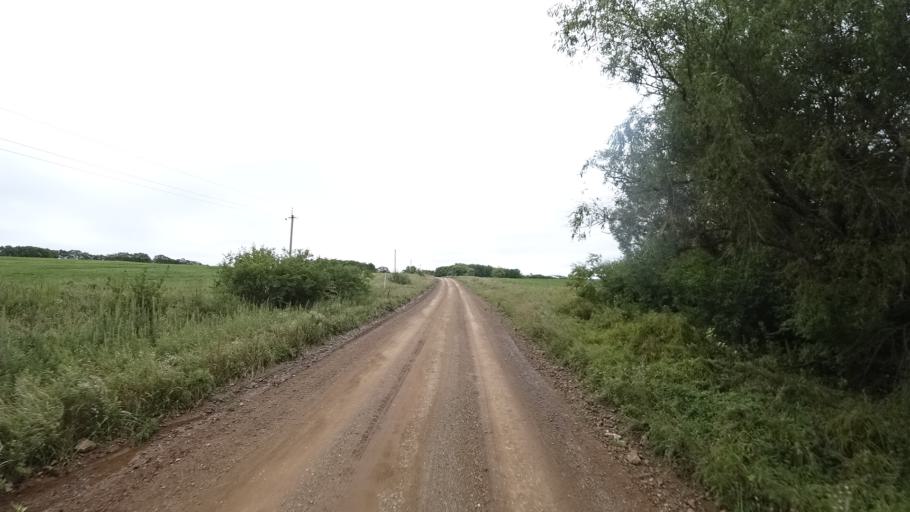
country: RU
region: Primorskiy
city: Lyalichi
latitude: 44.0627
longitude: 132.4776
